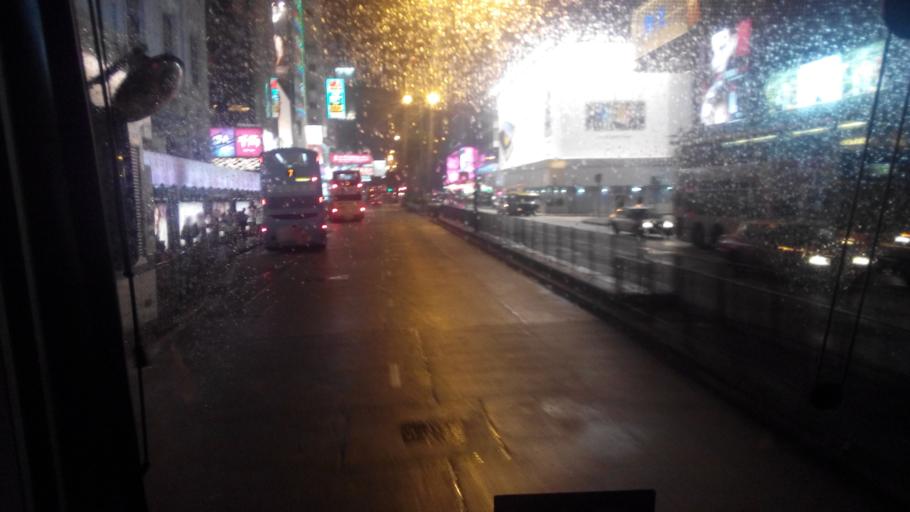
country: HK
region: Wanchai
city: Wan Chai
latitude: 22.2949
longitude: 114.1724
